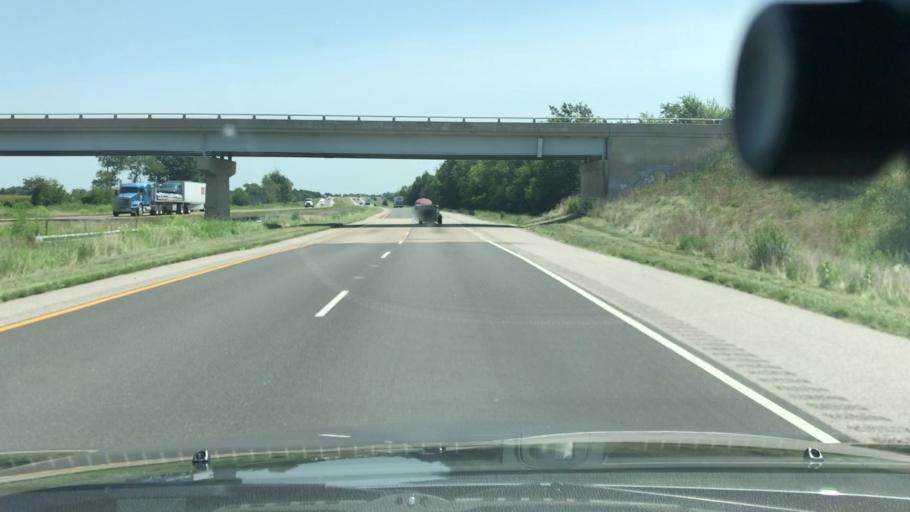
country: US
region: Illinois
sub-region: Clinton County
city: Wamac
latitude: 38.3886
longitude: -89.1922
